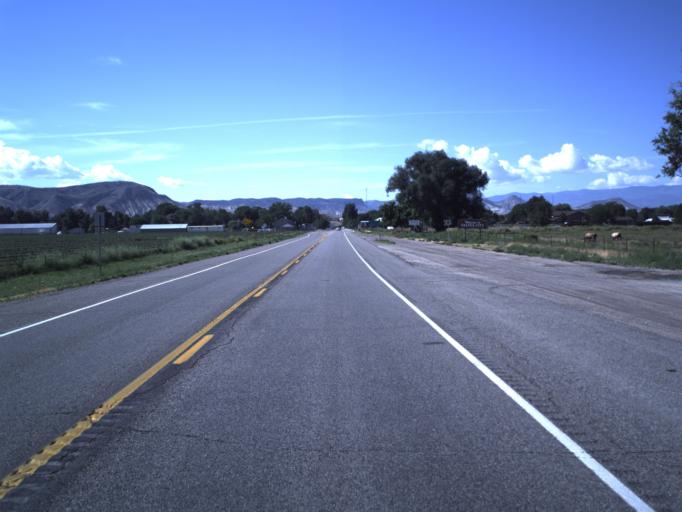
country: US
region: Utah
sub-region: Sevier County
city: Salina
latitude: 38.9691
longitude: -111.8601
